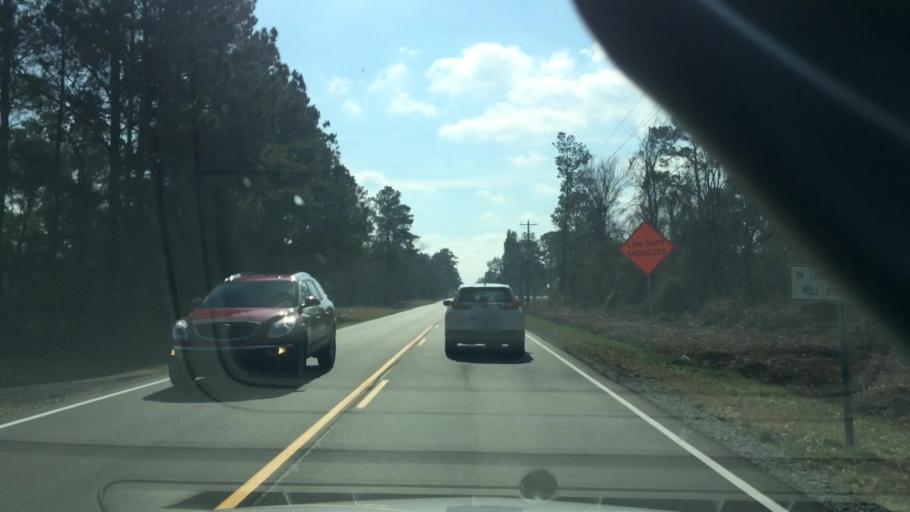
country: US
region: North Carolina
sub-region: Duplin County
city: Beulaville
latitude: 34.9783
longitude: -77.7604
